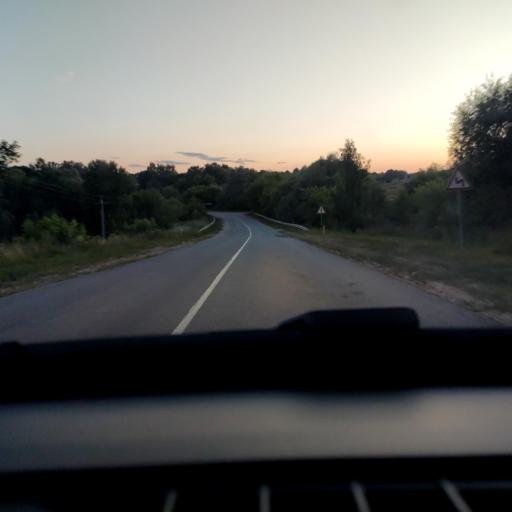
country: RU
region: Lipetsk
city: Zadonsk
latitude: 52.2922
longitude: 38.7644
